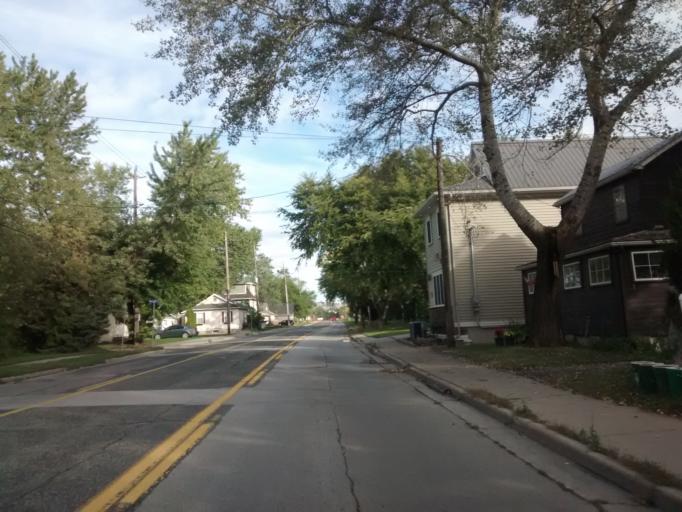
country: CA
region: Ontario
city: Hamilton
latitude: 43.3048
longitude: -79.7994
